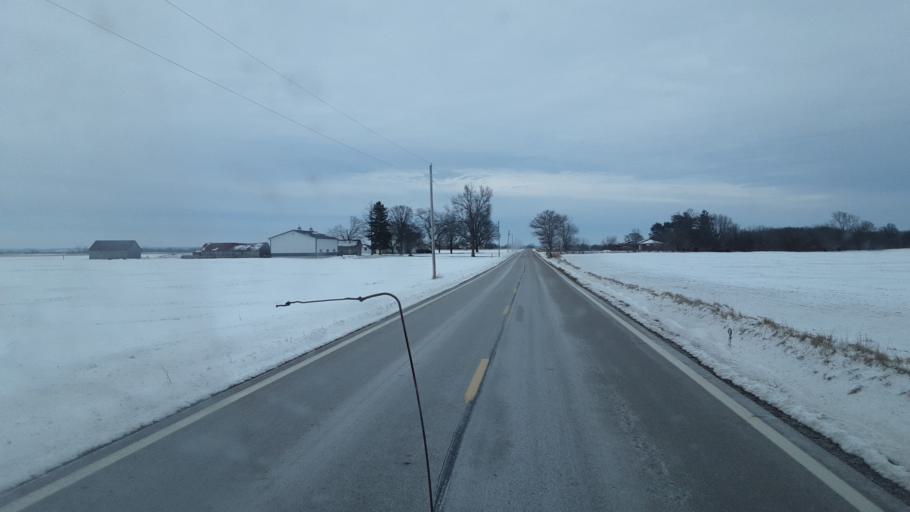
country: US
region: Ohio
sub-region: Pickaway County
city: Williamsport
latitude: 39.6348
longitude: -83.0720
